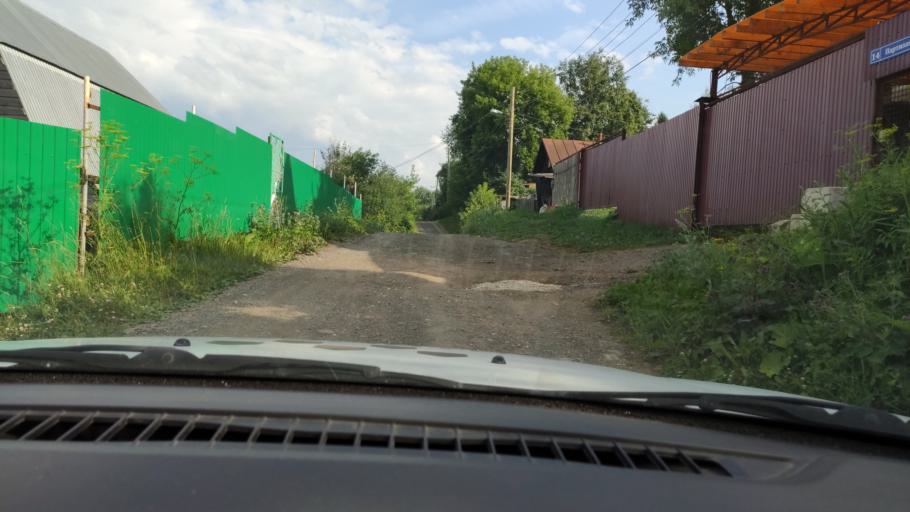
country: RU
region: Perm
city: Perm
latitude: 58.0338
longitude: 56.3311
